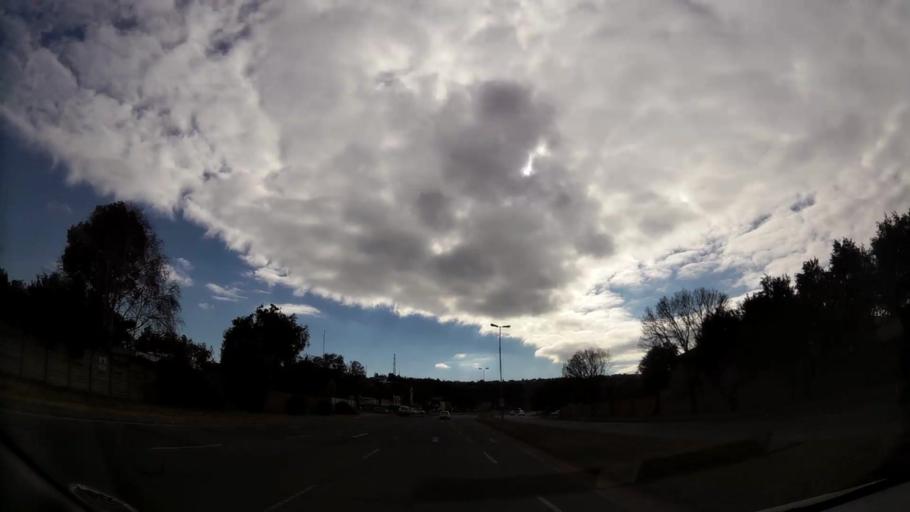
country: ZA
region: Gauteng
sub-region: City of Johannesburg Metropolitan Municipality
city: Roodepoort
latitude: -26.1098
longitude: 27.8552
